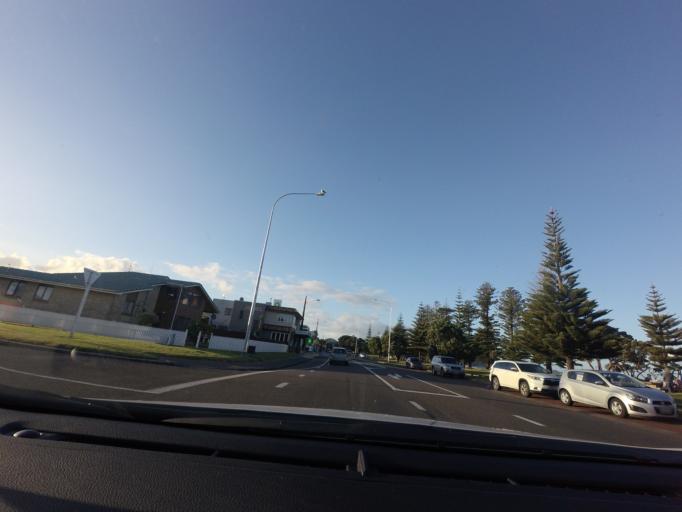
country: NZ
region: Auckland
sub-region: Auckland
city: Rothesay Bay
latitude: -36.5906
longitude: 174.6980
